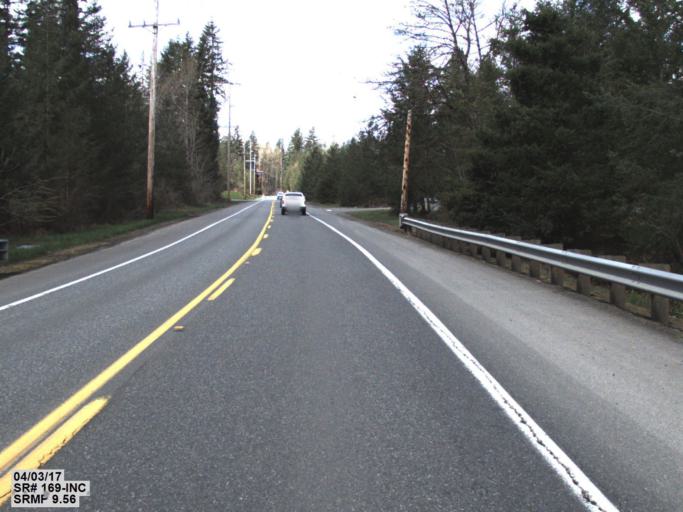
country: US
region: Washington
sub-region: King County
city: Black Diamond
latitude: 47.3353
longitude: -122.0131
